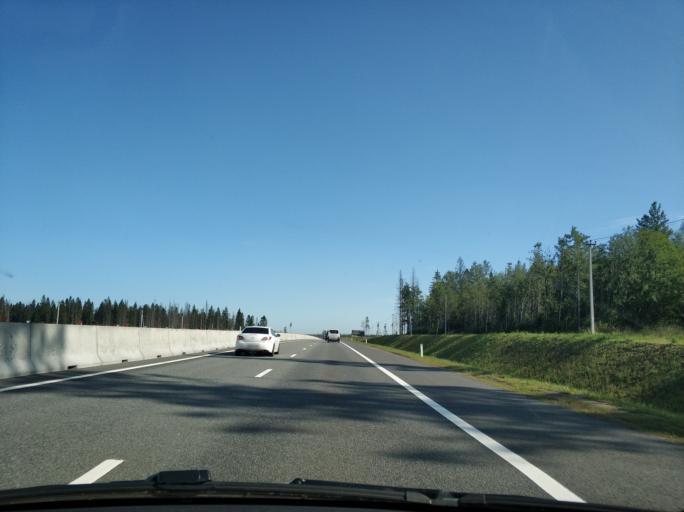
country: RU
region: Leningrad
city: Sosnovo
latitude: 60.4902
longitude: 30.1958
